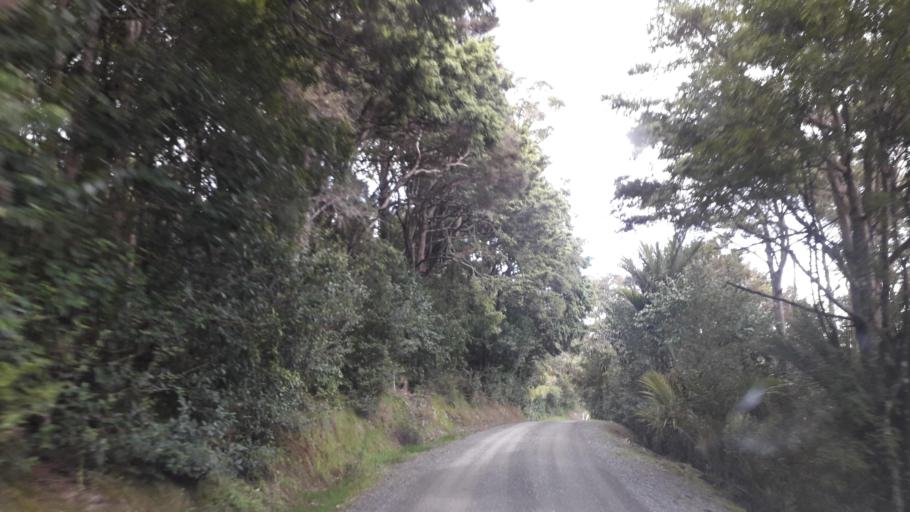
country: NZ
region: Northland
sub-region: Far North District
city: Waimate North
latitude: -35.3074
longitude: 173.5640
